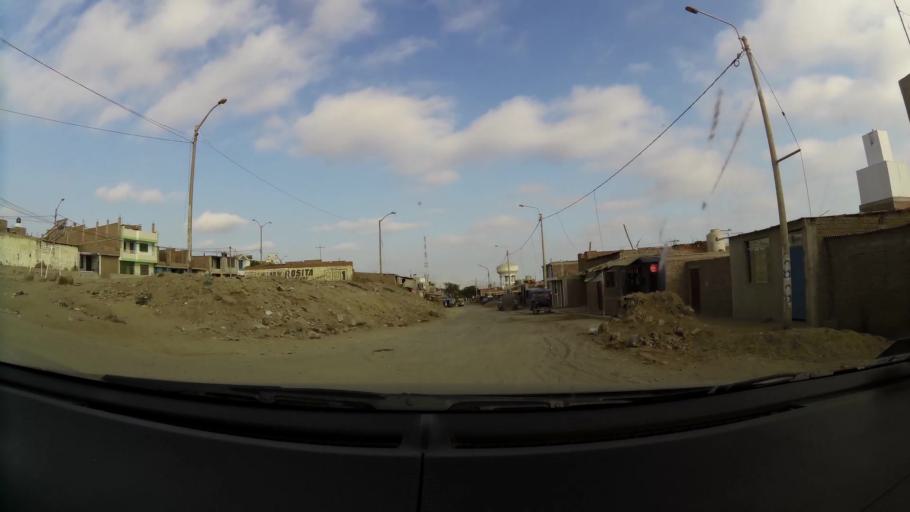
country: PE
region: La Libertad
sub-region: Provincia de Trujillo
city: La Esperanza
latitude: -8.0726
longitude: -79.0417
